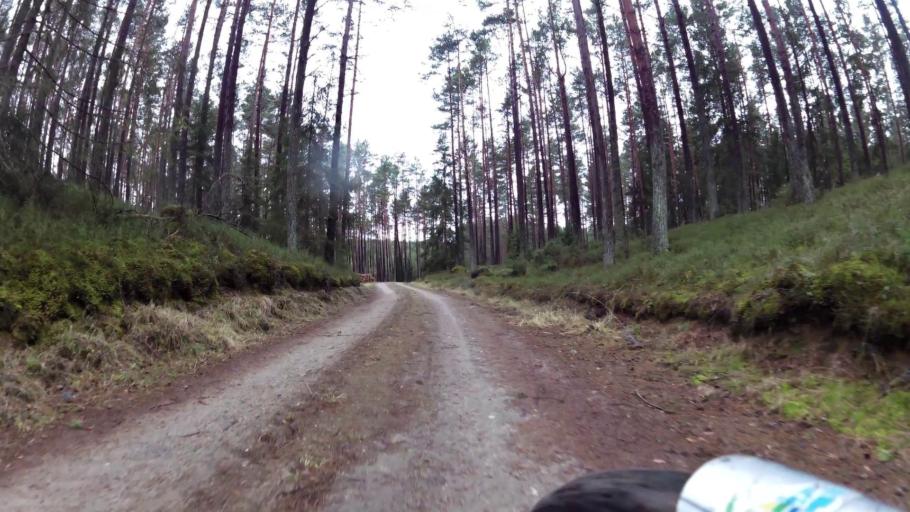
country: PL
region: Pomeranian Voivodeship
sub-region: Powiat bytowski
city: Borzytuchom
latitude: 54.2602
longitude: 17.3837
